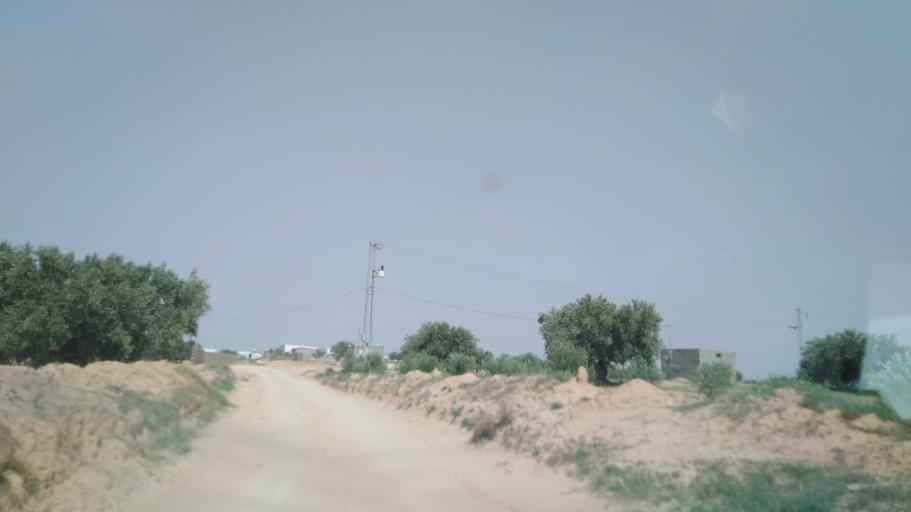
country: TN
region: Safaqis
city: Sfax
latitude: 34.6240
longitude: 10.5767
